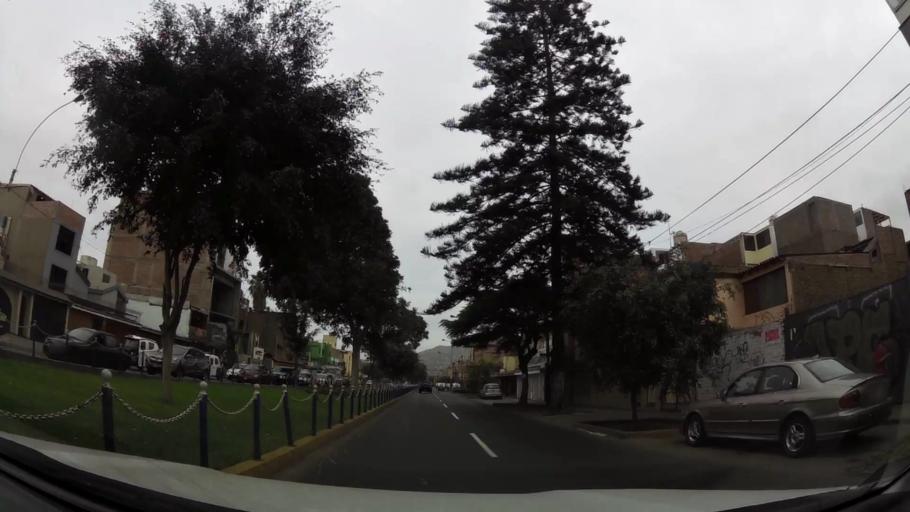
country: PE
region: Lima
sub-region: Lima
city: Surco
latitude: -12.1771
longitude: -77.0078
